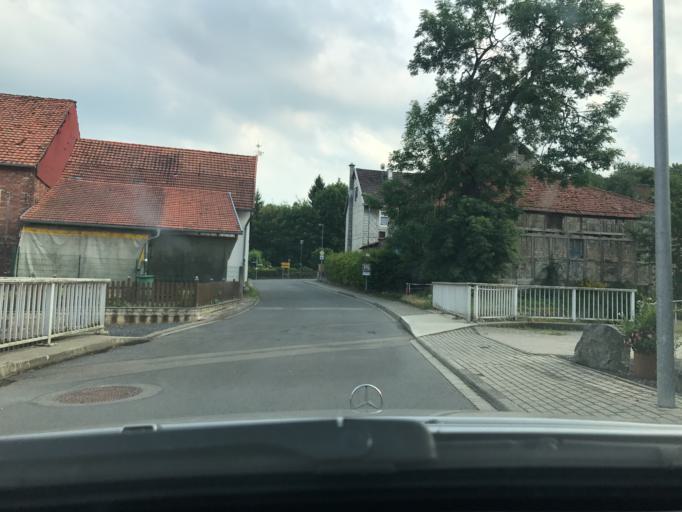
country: DE
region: Thuringia
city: Kefferhausen
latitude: 51.3146
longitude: 10.2817
